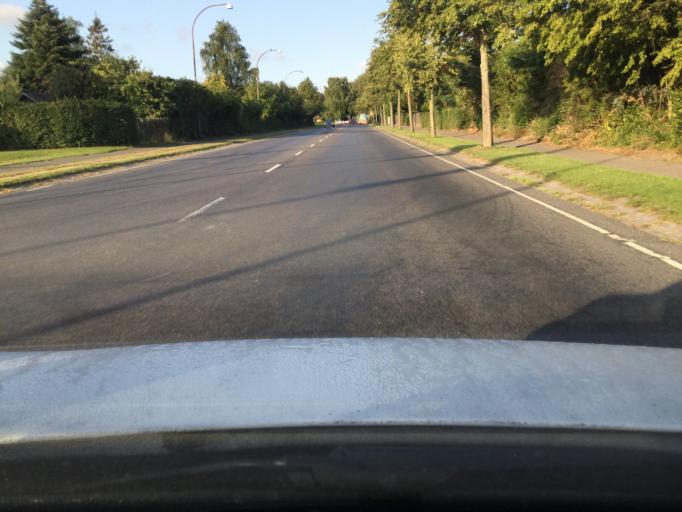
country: DK
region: Zealand
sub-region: Lolland Kommune
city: Nakskov
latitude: 54.8237
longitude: 11.1567
